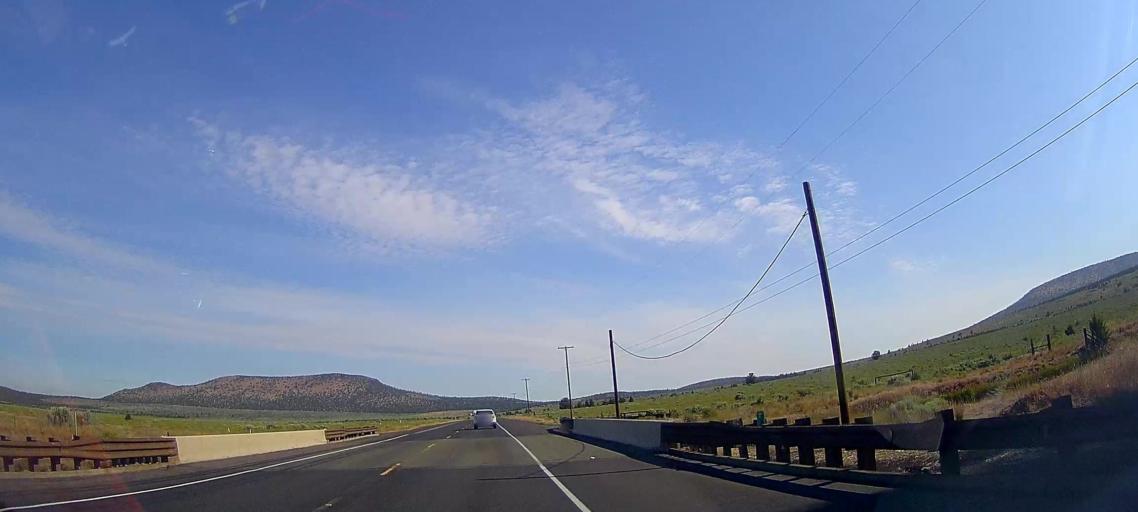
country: US
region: Oregon
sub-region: Jefferson County
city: Culver
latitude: 44.4445
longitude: -121.1993
